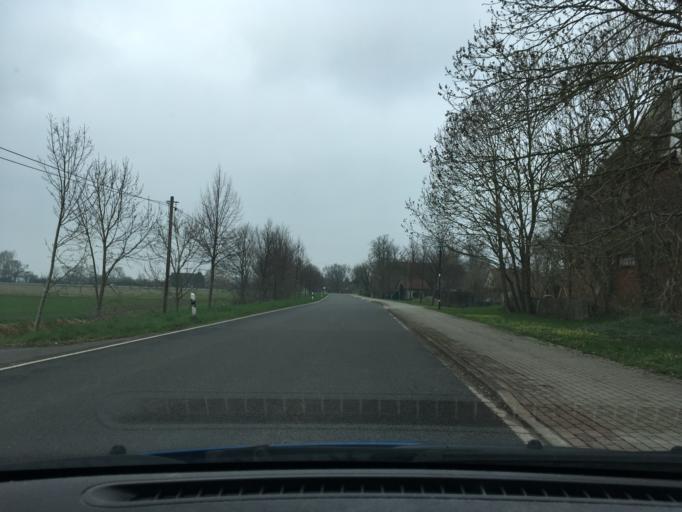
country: DE
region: Lower Saxony
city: Neu Darchau
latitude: 53.3085
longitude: 10.8905
